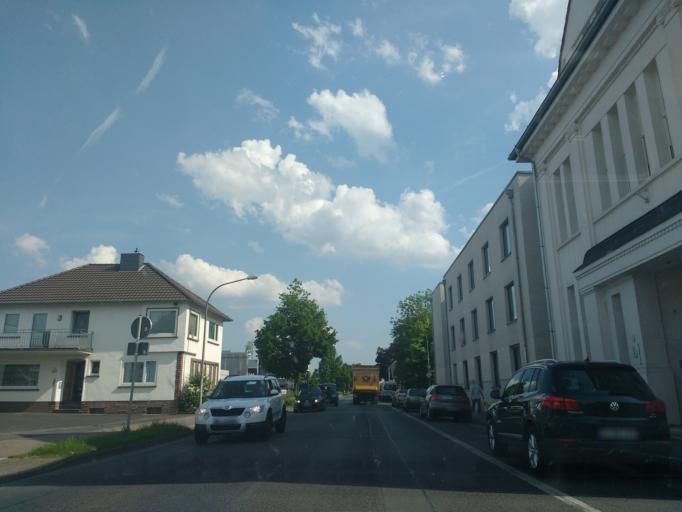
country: DE
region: North Rhine-Westphalia
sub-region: Regierungsbezirk Detmold
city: Lage
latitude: 51.9889
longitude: 8.8022
